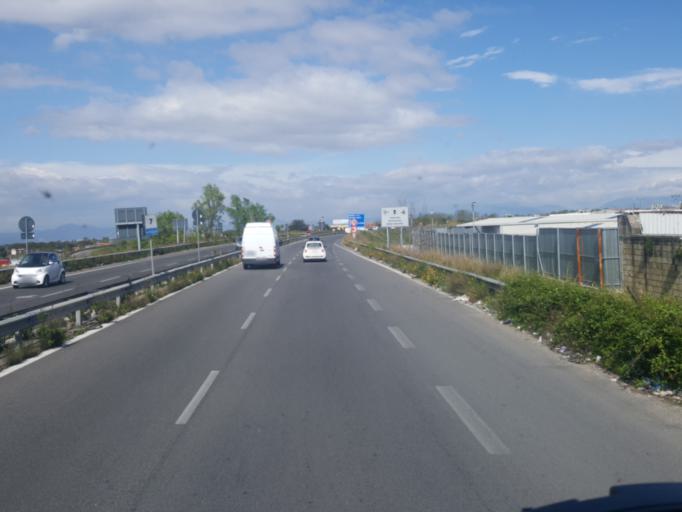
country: IT
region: Campania
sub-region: Provincia di Napoli
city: Qualiano
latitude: 40.9321
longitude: 14.1364
